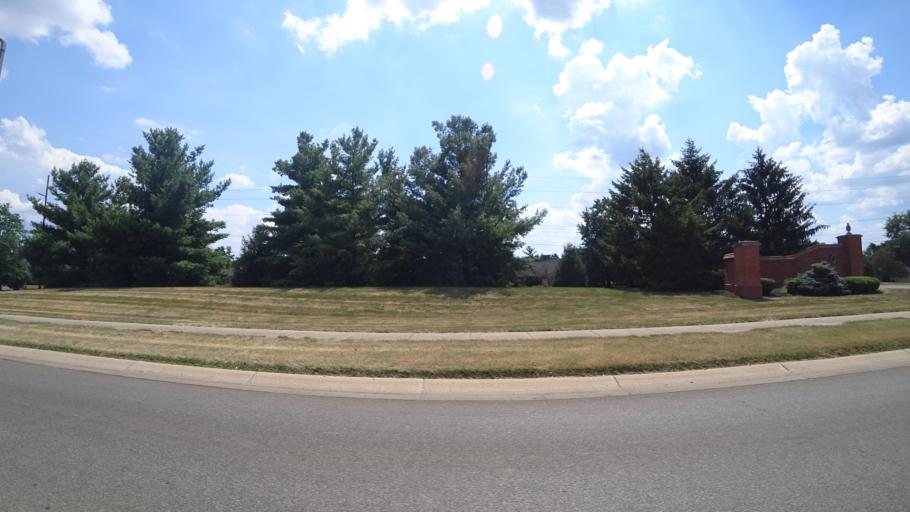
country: US
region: Ohio
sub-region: Butler County
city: Hamilton
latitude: 39.4232
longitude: -84.5605
